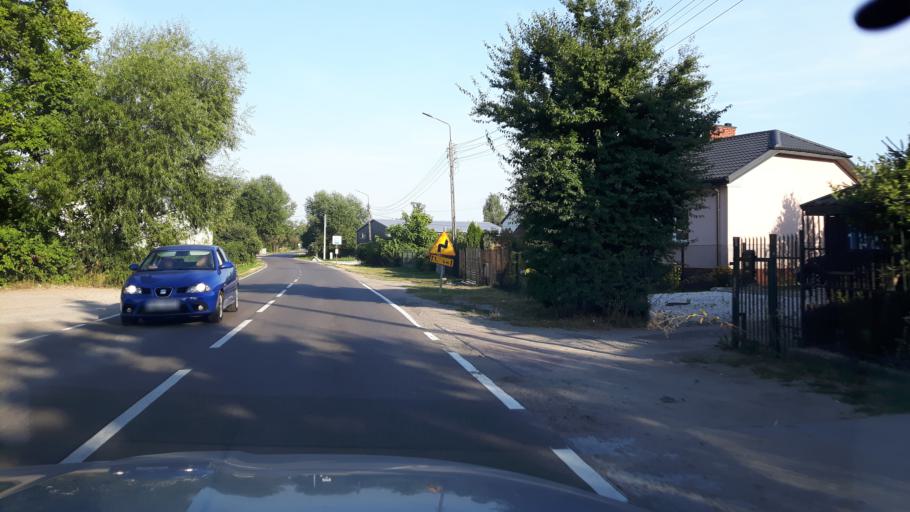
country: PL
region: Masovian Voivodeship
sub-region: Powiat wolominski
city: Slupno
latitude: 52.3615
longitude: 21.1674
